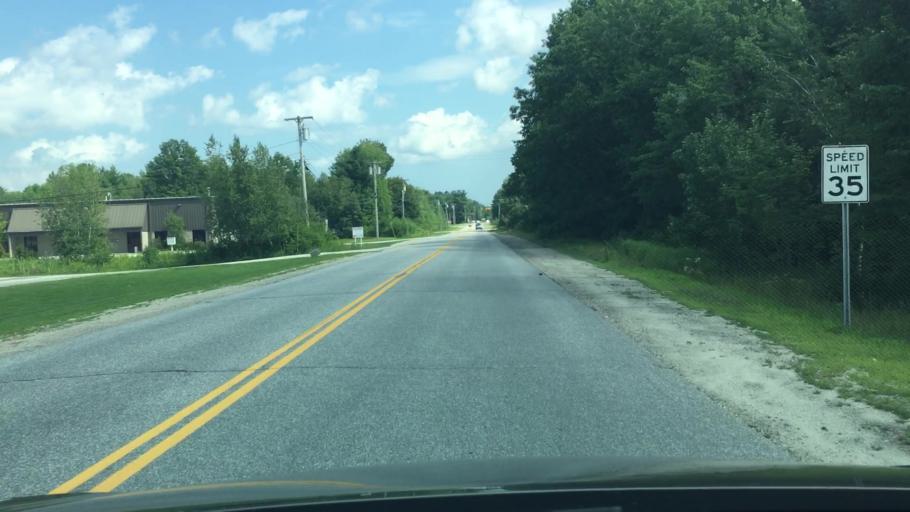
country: US
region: Maine
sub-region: Androscoggin County
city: Auburn
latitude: 44.0794
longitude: -70.2622
